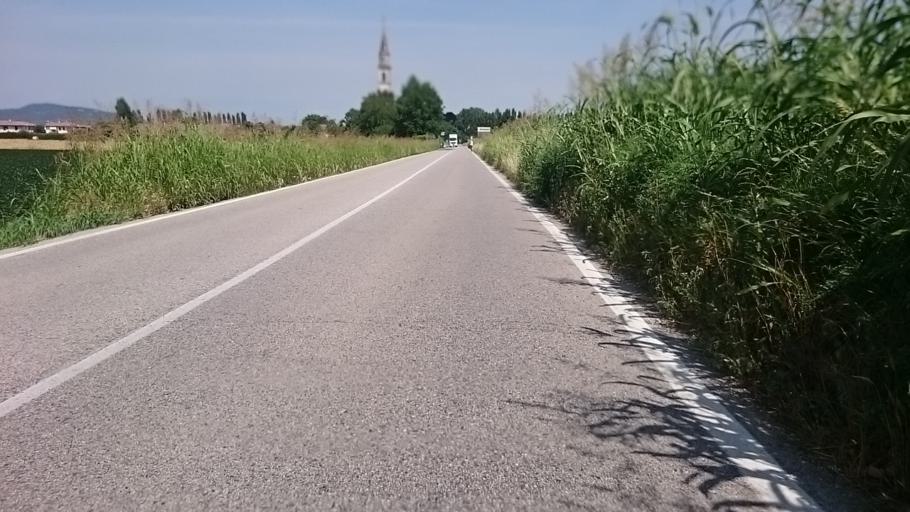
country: IT
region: Veneto
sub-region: Provincia di Vicenza
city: Montegaldella
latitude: 45.4327
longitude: 11.6769
